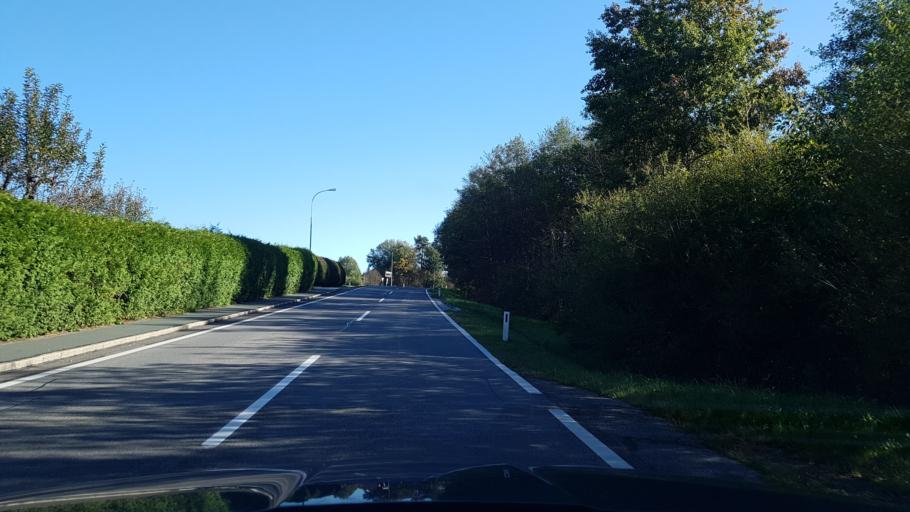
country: AT
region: Styria
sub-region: Politischer Bezirk Leibnitz
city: Gleinstatten
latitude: 46.7482
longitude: 15.3470
